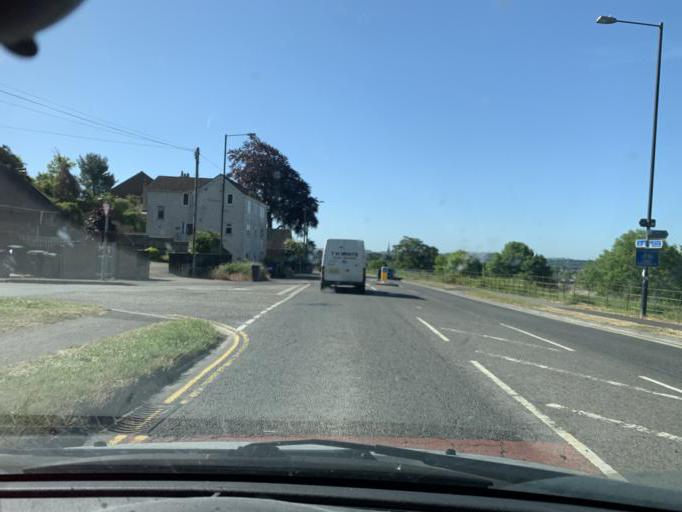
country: GB
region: England
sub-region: Wiltshire
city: Salisbury
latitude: 51.0910
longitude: -1.7999
